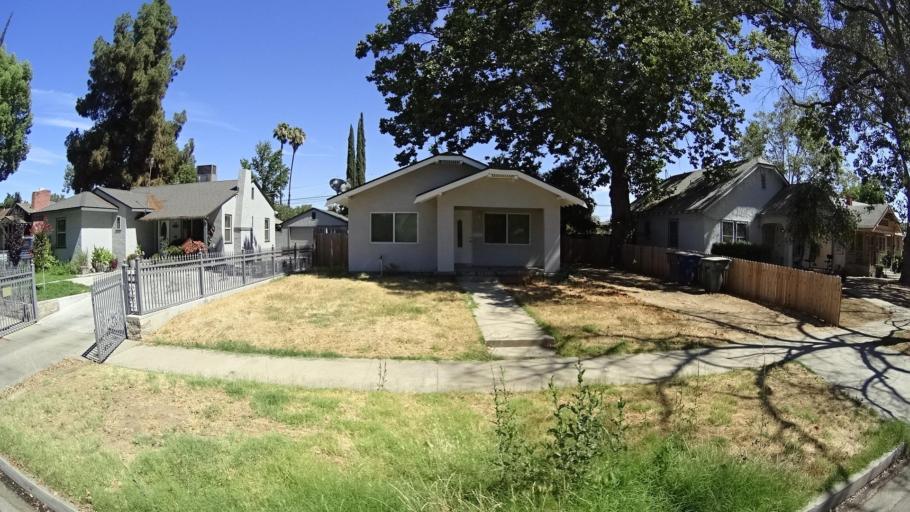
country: US
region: California
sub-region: Fresno County
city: Fresno
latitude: 36.7459
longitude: -119.7466
